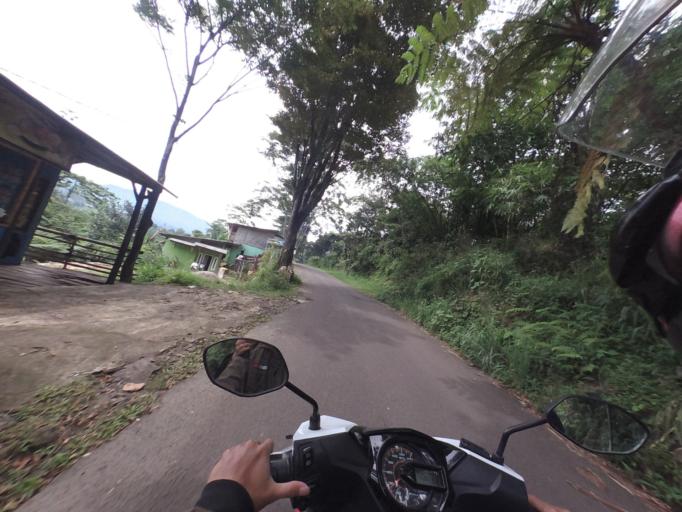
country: ID
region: West Java
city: Ciampea
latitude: -6.6854
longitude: 106.6775
